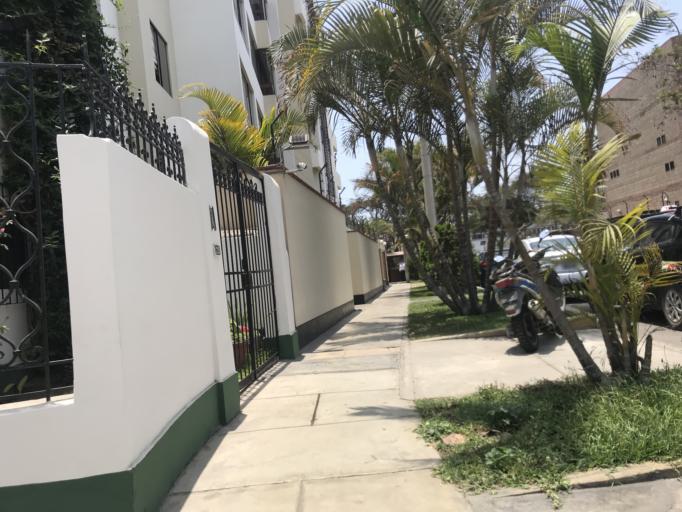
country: PE
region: Lima
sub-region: Lima
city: San Isidro
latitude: -12.1059
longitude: -77.0327
